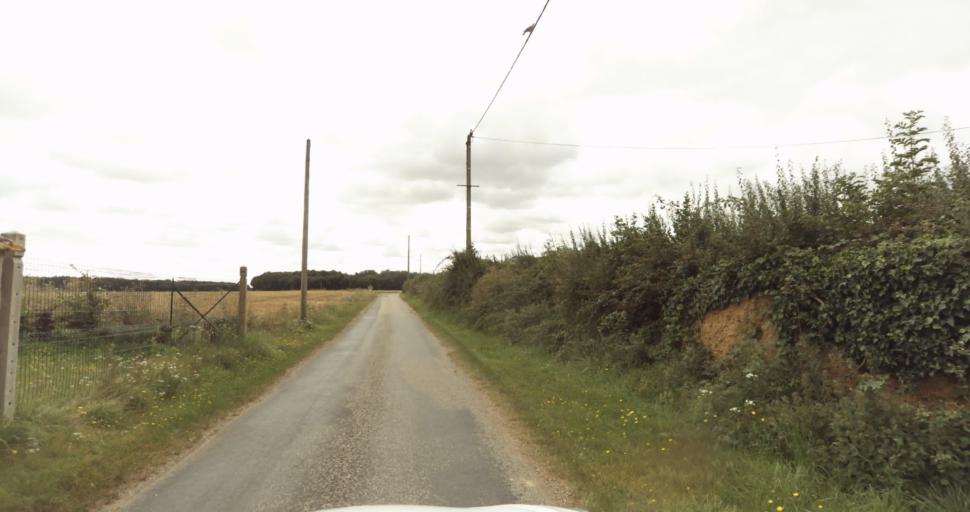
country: FR
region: Haute-Normandie
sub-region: Departement de l'Eure
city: Nonancourt
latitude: 48.7959
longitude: 1.1323
